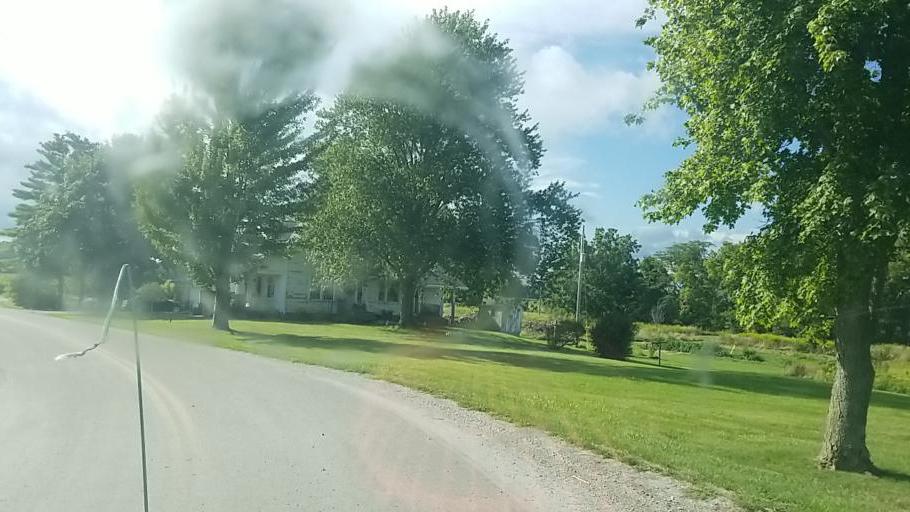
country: US
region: Ohio
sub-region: Hardin County
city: Forest
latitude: 40.7296
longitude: -83.5146
